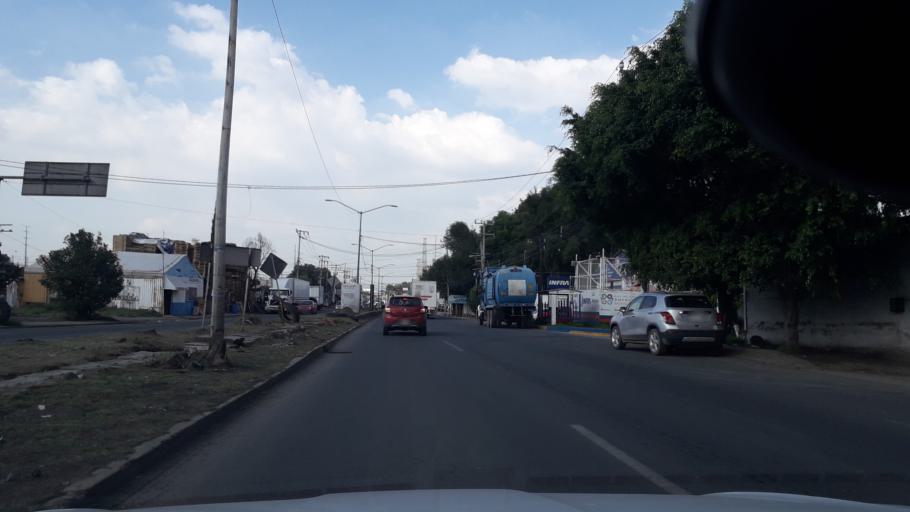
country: MX
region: Mexico
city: Tultitlan
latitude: 19.6315
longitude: -99.1847
